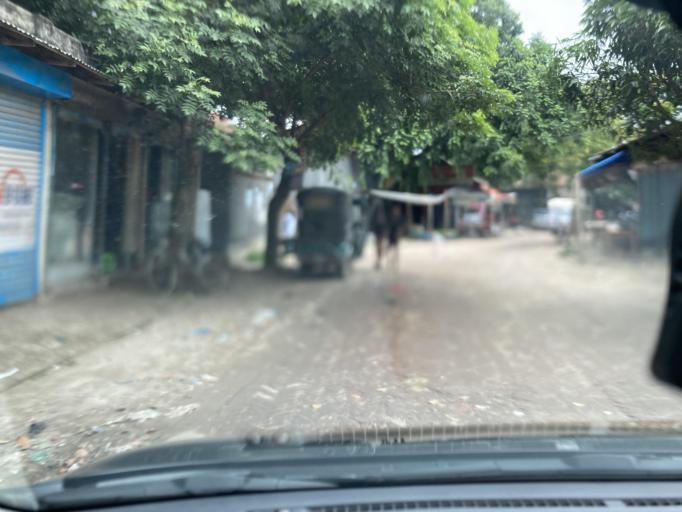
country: BD
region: Dhaka
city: Dohar
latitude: 23.7959
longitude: 90.0511
